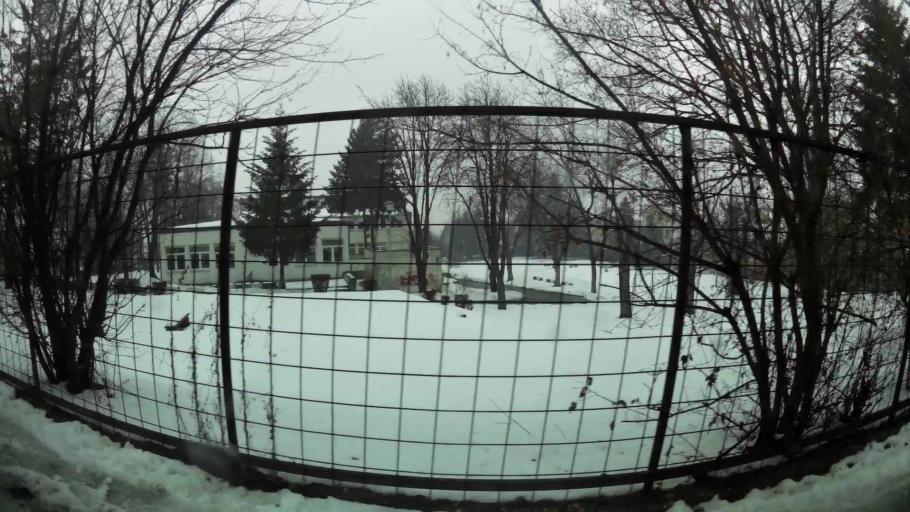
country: RS
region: Central Serbia
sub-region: Belgrade
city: Zvezdara
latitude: 44.7793
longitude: 20.5231
